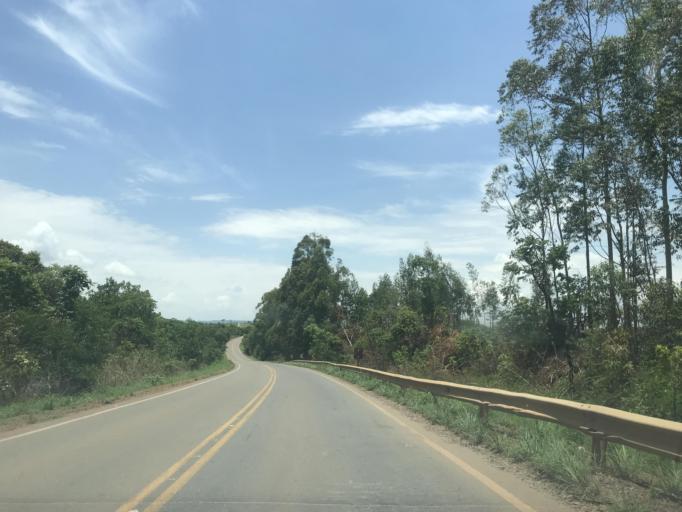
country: BR
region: Goias
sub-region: Vianopolis
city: Vianopolis
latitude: -16.5995
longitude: -48.3490
